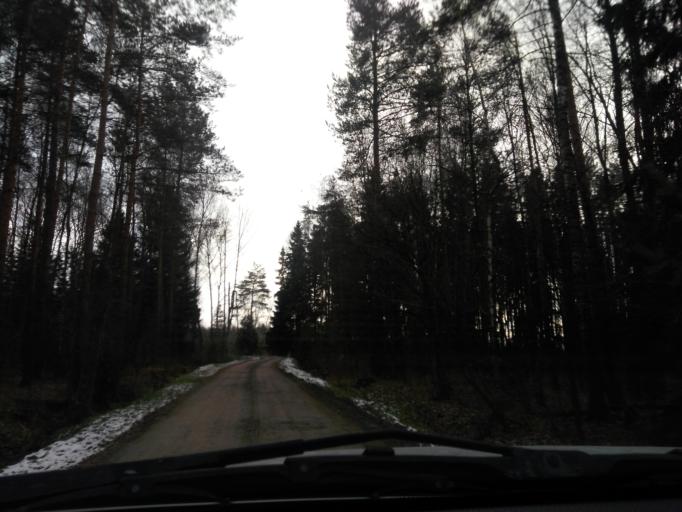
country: RU
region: Moskovskaya
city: Troitsk
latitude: 55.3705
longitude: 37.1638
